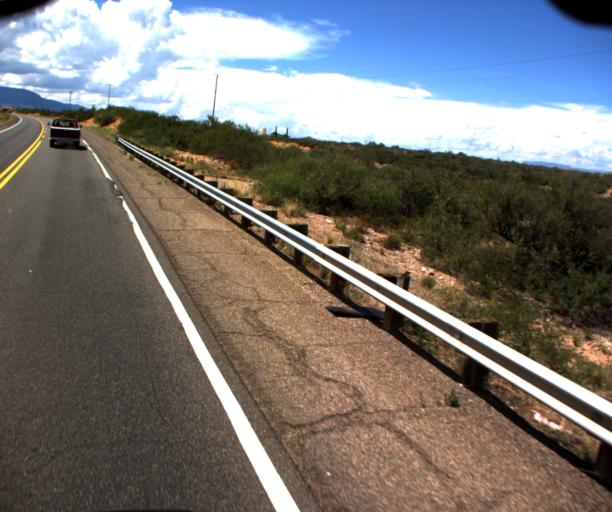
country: US
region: Arizona
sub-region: Yavapai County
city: Camp Verde
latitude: 34.5970
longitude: -111.8947
